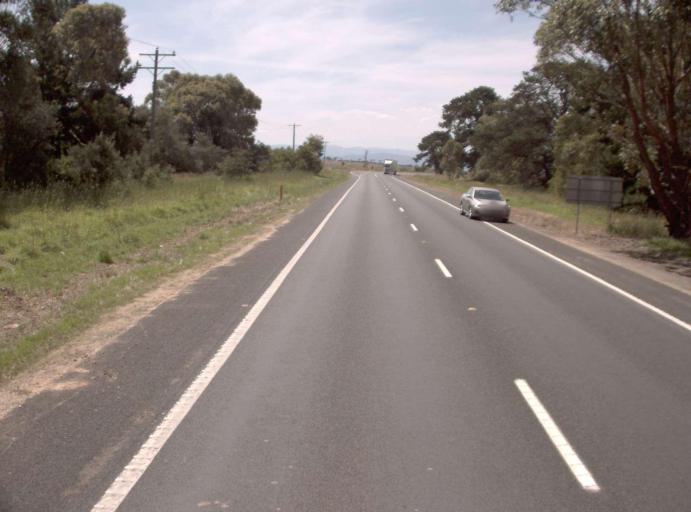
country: AU
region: Victoria
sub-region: Wellington
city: Sale
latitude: -38.0354
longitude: 147.0591
